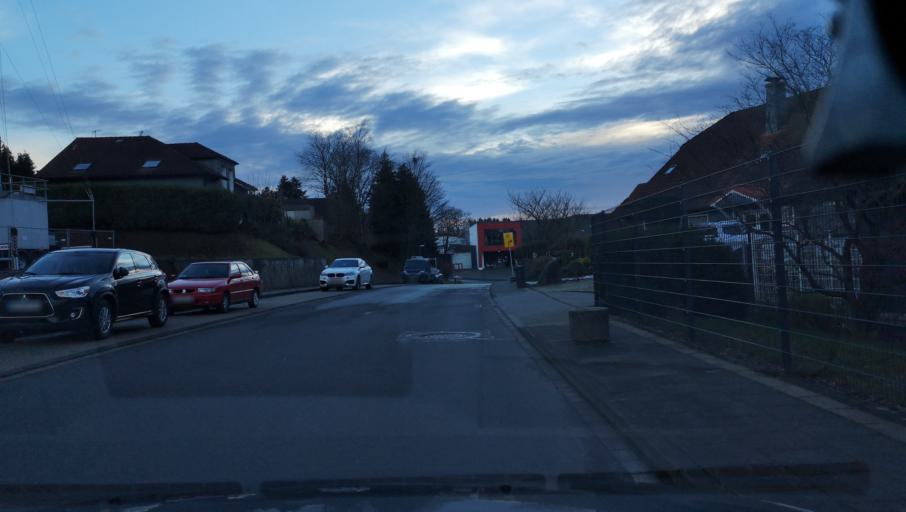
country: DE
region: North Rhine-Westphalia
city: Radevormwald
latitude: 51.2007
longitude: 7.3838
